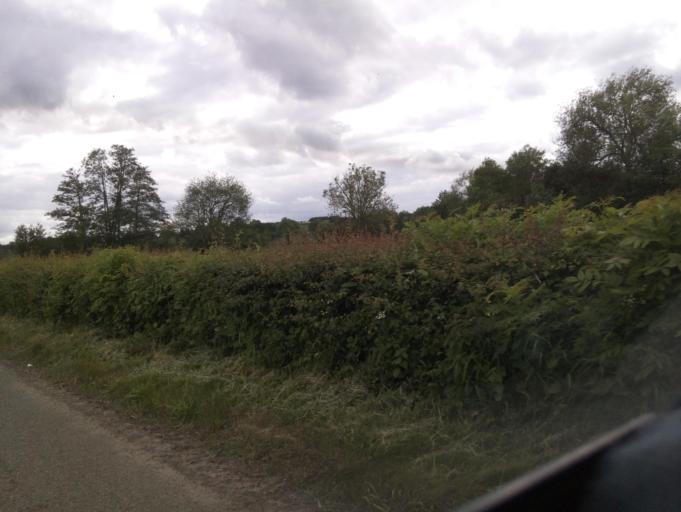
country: GB
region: England
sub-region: Herefordshire
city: Yatton
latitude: 51.9940
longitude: -2.5036
